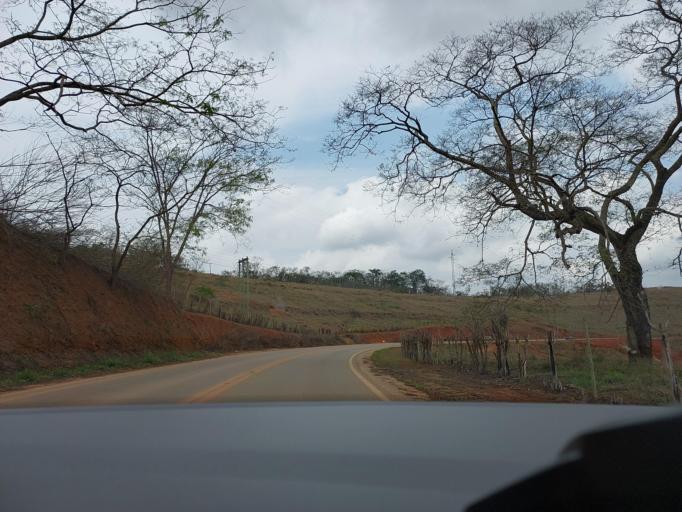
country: BR
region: Minas Gerais
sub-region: Ponte Nova
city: Ponte Nova
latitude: -20.3903
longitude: -42.8703
